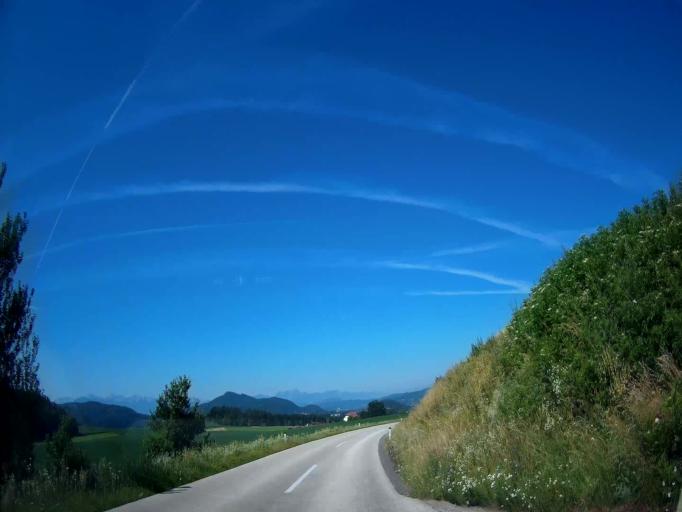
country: AT
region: Carinthia
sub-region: Politischer Bezirk Klagenfurt Land
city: Maria Saal
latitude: 46.6966
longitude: 14.3921
